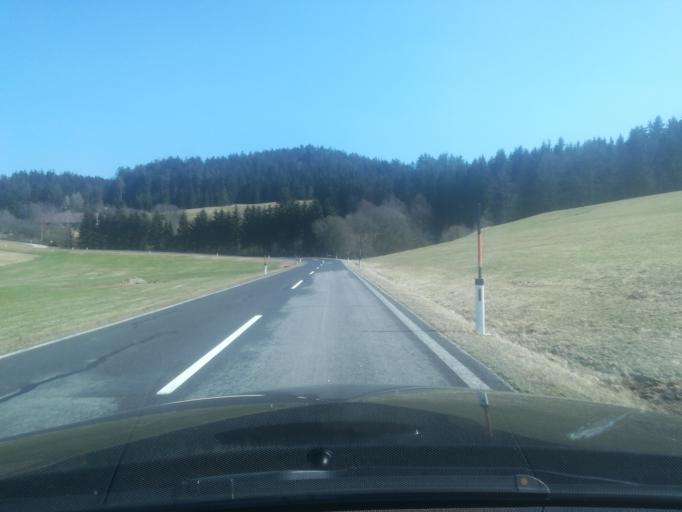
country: AT
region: Lower Austria
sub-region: Politischer Bezirk Zwettl
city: Langschlag
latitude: 48.4943
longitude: 14.8182
